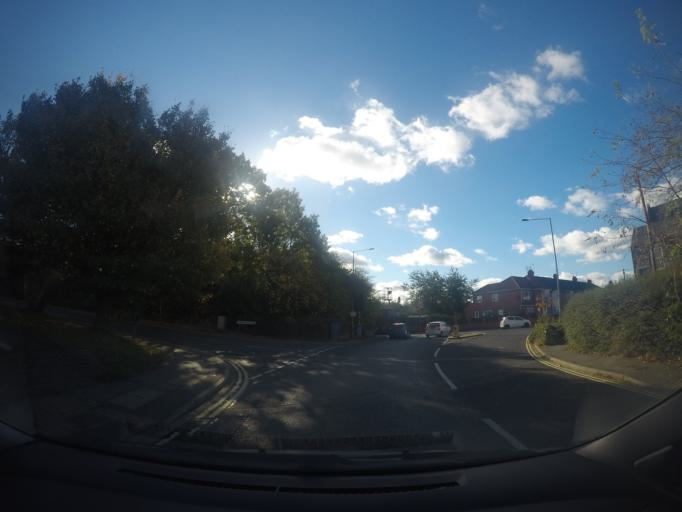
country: GB
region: England
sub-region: City of York
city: York
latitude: 53.9629
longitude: -1.1050
